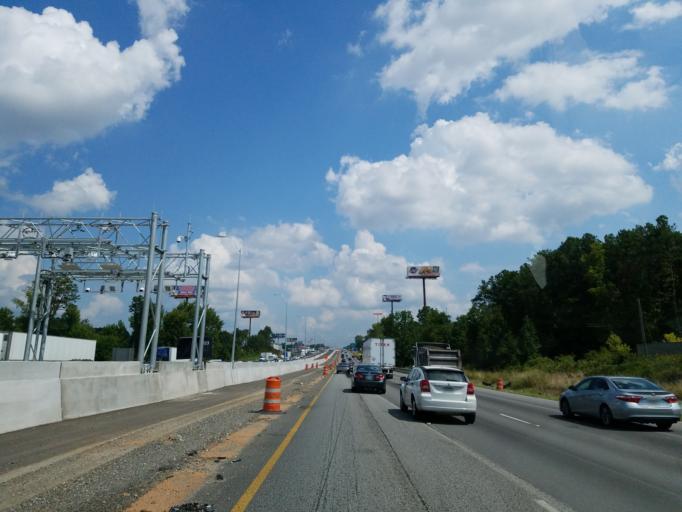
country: US
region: Georgia
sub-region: Henry County
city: McDonough
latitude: 33.4232
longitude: -84.1765
